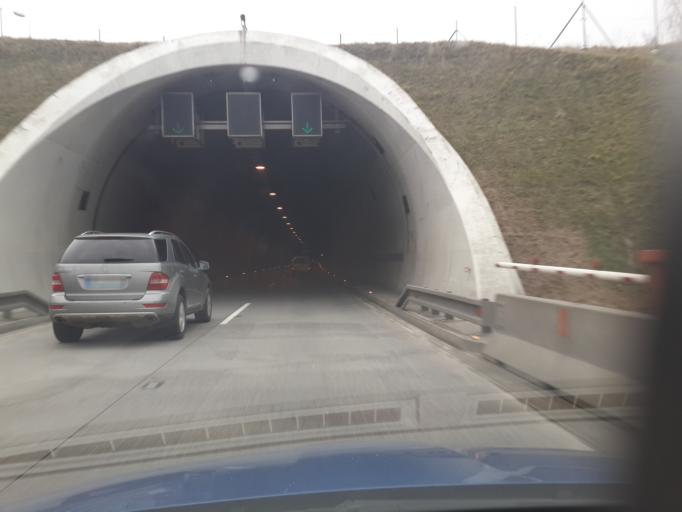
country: SK
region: Bratislavsky
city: Bratislava
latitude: 48.1737
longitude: 17.0637
